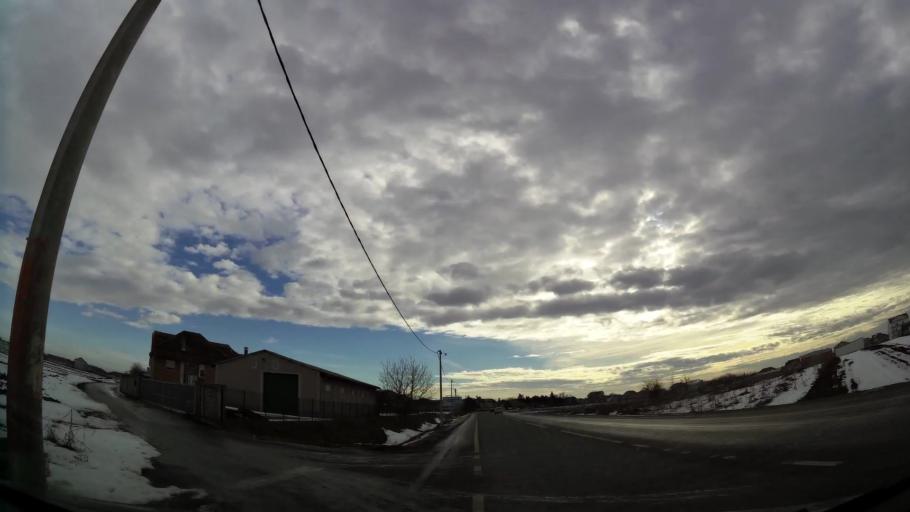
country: RS
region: Central Serbia
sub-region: Belgrade
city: Surcin
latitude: 44.8017
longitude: 20.3167
